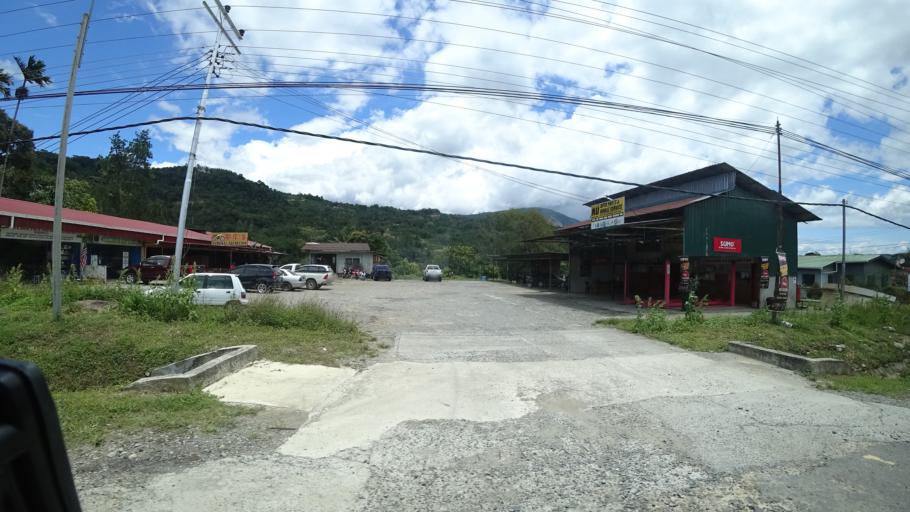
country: MY
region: Sabah
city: Ranau
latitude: 5.9539
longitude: 116.6615
